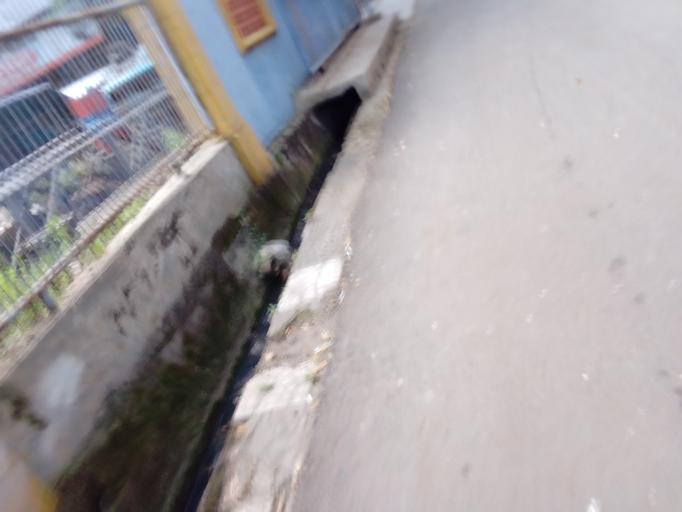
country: ID
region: Jakarta Raya
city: Jakarta
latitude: -6.2180
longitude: 106.7927
